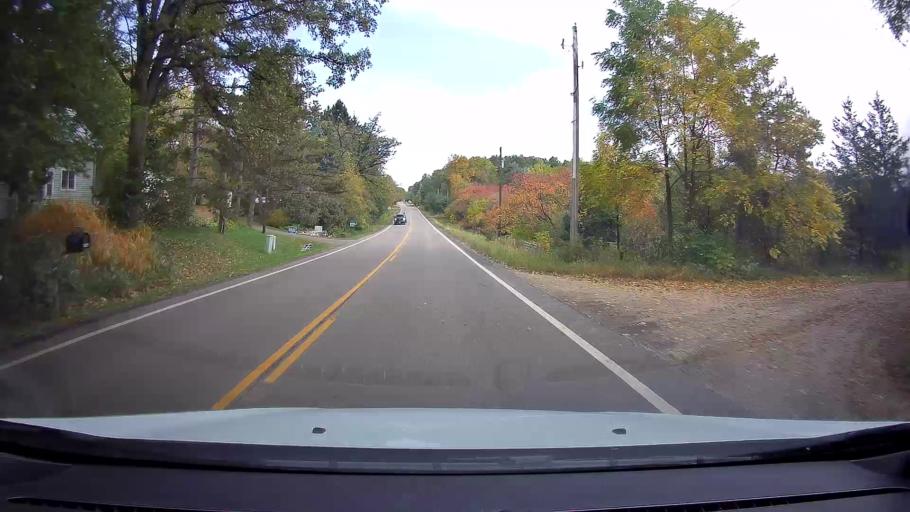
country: US
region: Minnesota
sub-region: Washington County
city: Stillwater
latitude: 45.0827
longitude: -92.8255
